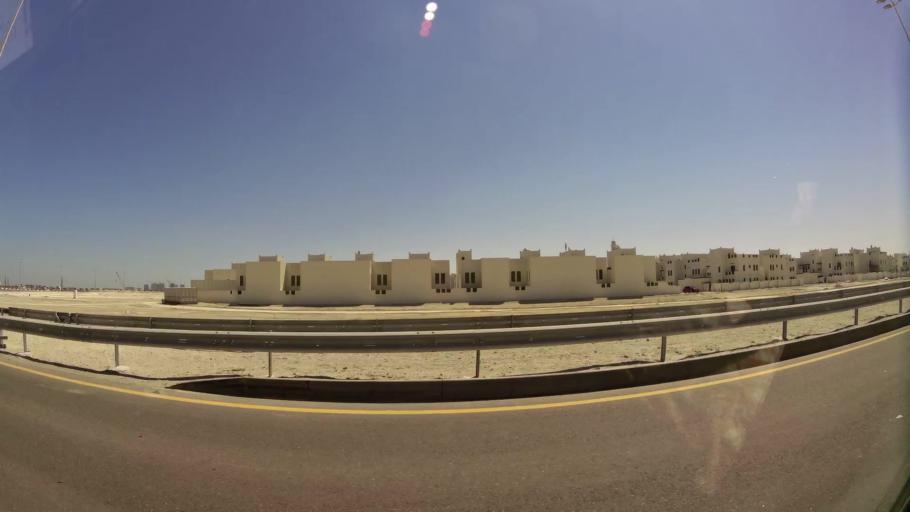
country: BH
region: Muharraq
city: Al Muharraq
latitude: 26.3043
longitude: 50.6379
